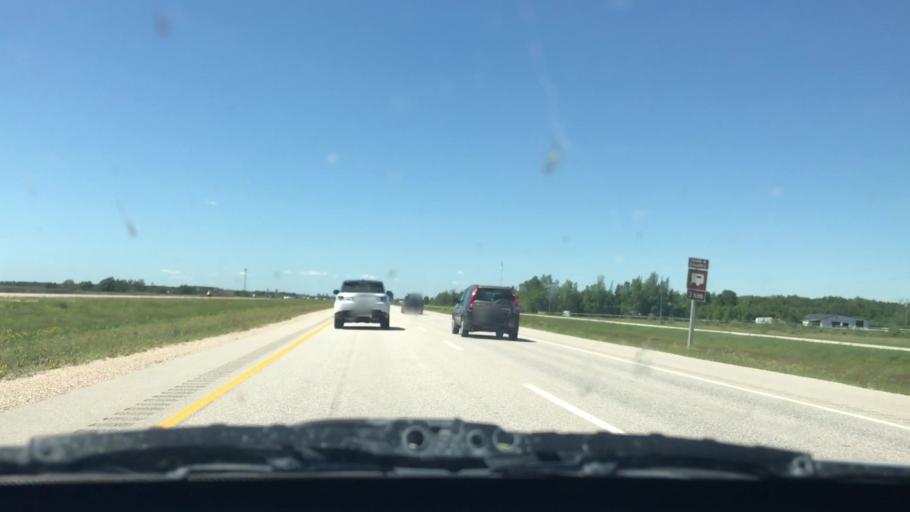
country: CA
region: Manitoba
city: Winnipeg
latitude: 49.8136
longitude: -96.9193
